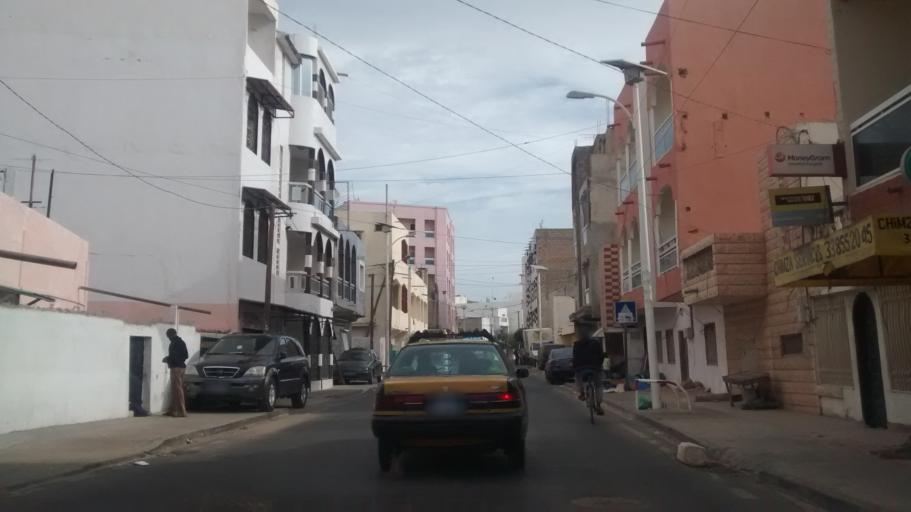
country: SN
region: Dakar
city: Pikine
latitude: 14.7596
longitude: -17.4228
